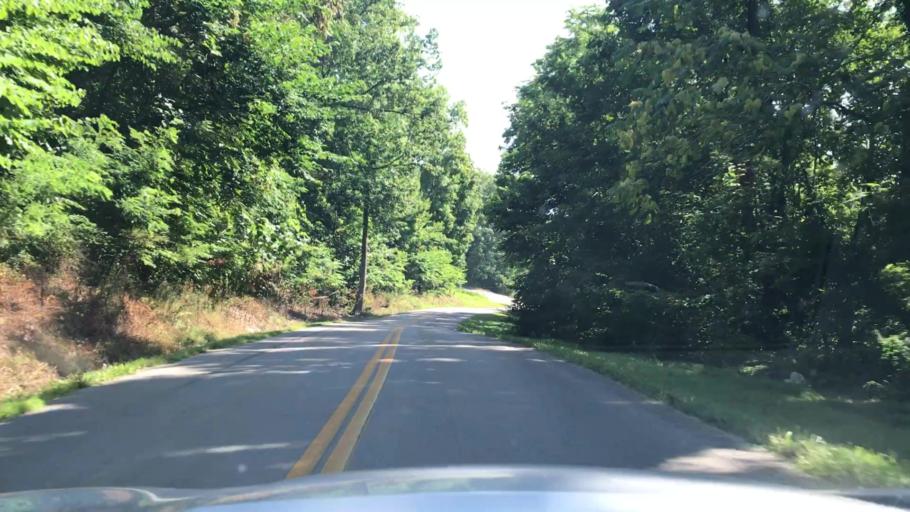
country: US
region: Kentucky
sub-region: Clinton County
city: Albany
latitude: 36.7224
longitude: -85.0199
